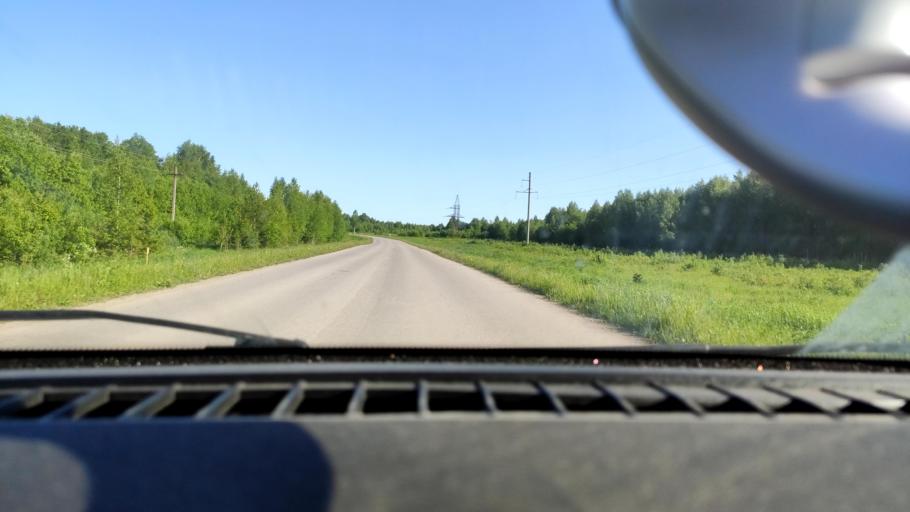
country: RU
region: Perm
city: Polazna
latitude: 58.2052
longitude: 56.5309
